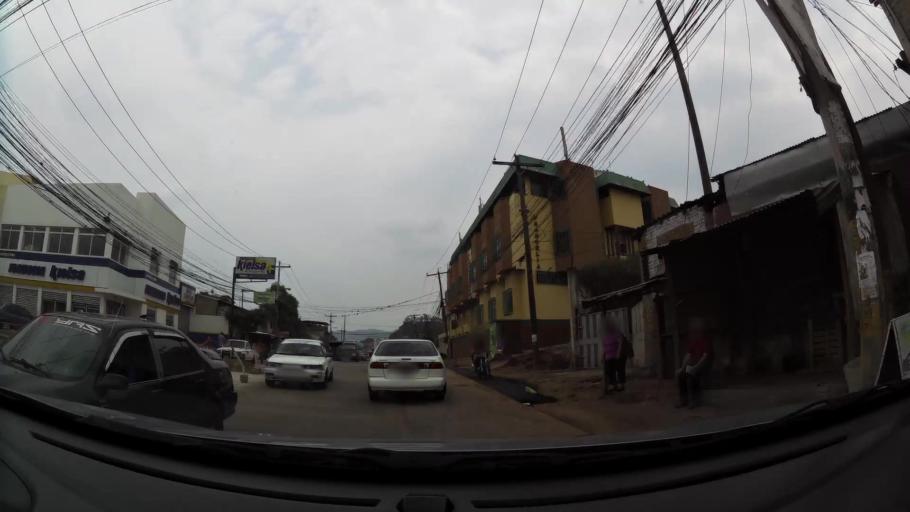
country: HN
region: Francisco Morazan
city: Tegucigalpa
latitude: 14.0688
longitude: -87.2133
